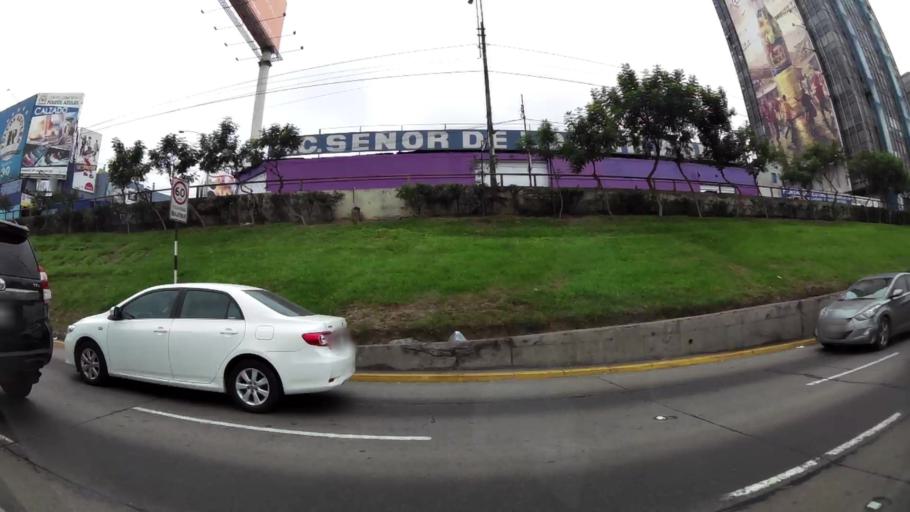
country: PE
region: Lima
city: Lima
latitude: -12.0626
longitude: -77.0343
